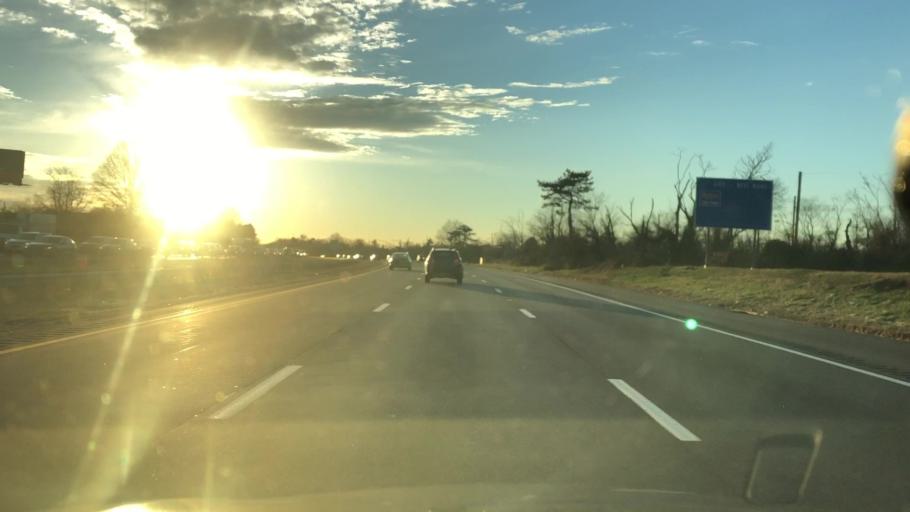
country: US
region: New Jersey
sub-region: Middlesex County
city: South Plainfield
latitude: 40.5580
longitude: -74.4274
